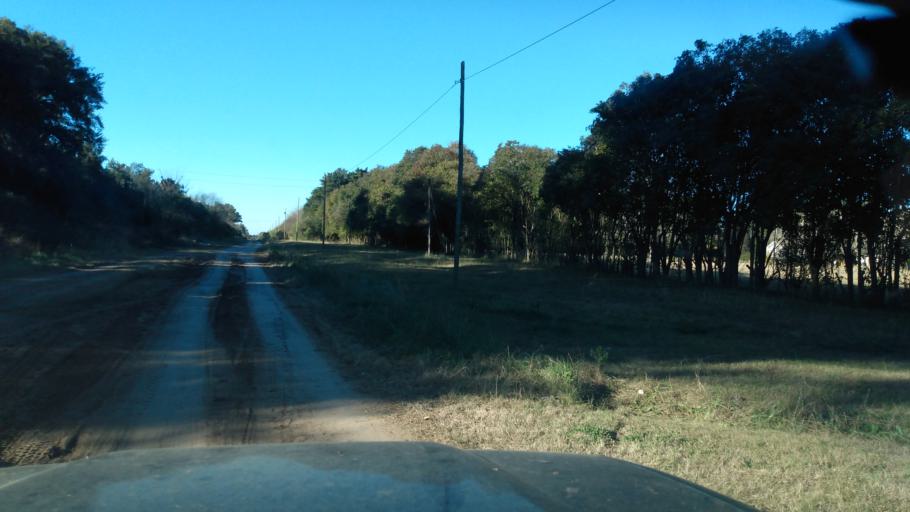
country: AR
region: Buenos Aires
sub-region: Partido de Lujan
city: Lujan
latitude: -34.5566
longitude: -59.1532
